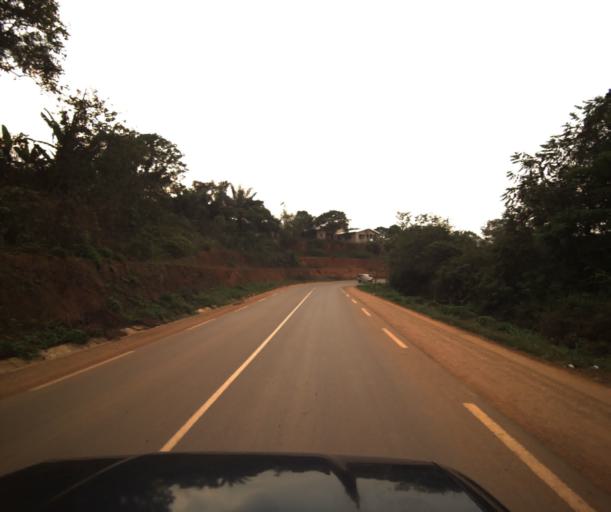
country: CM
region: Centre
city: Yaounde
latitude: 3.8061
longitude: 11.4639
